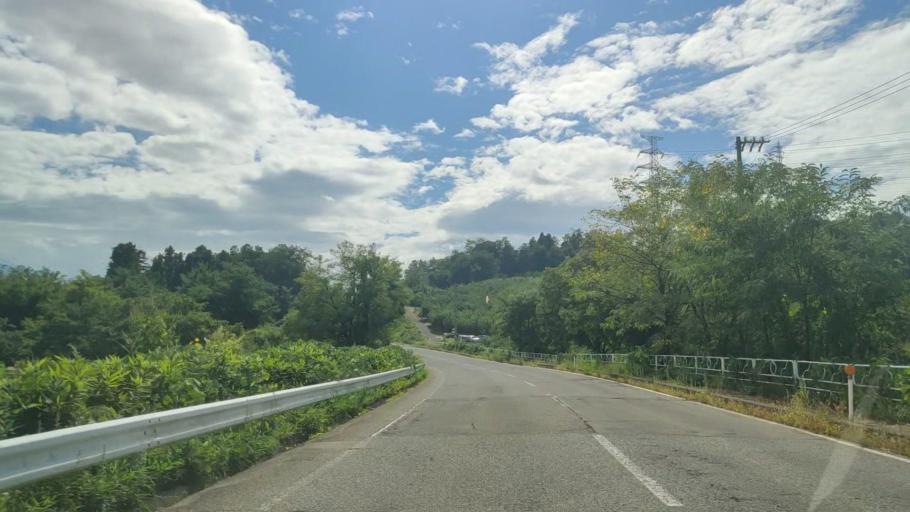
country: JP
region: Nagano
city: Nakano
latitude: 36.7366
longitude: 138.3051
